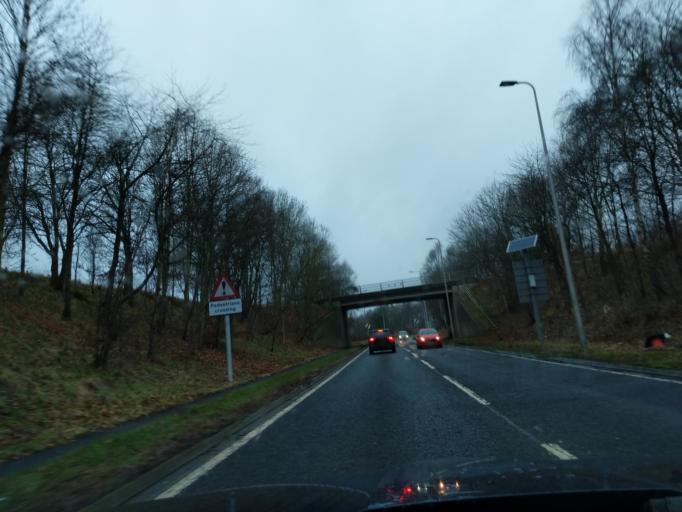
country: GB
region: Scotland
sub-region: The Scottish Borders
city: Melrose
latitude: 55.6003
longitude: -2.7485
